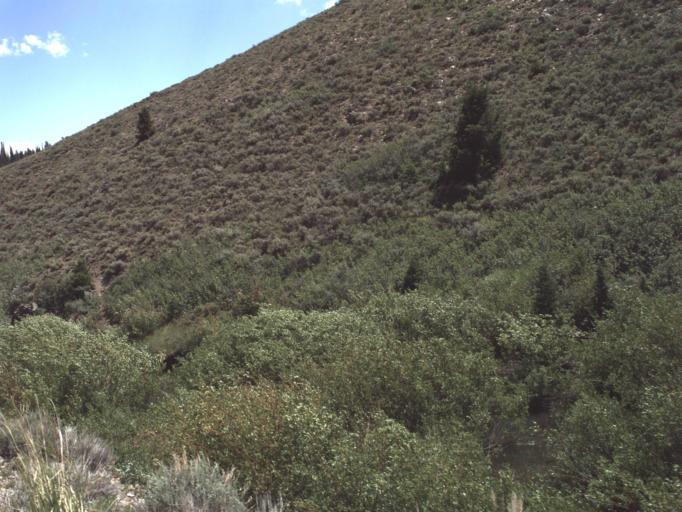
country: US
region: Utah
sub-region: Rich County
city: Randolph
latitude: 41.4846
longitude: -111.3966
